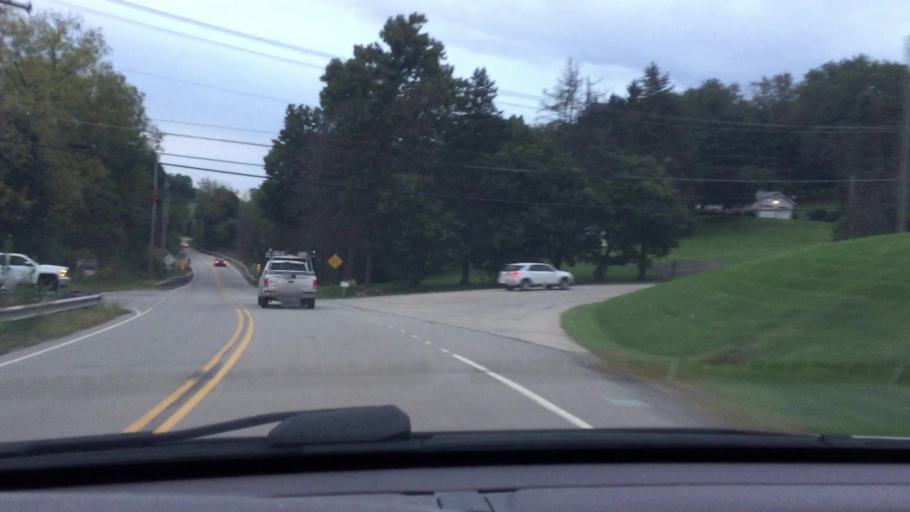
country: US
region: Pennsylvania
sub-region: Westmoreland County
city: Fellsburg
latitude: 40.1884
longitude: -79.7965
